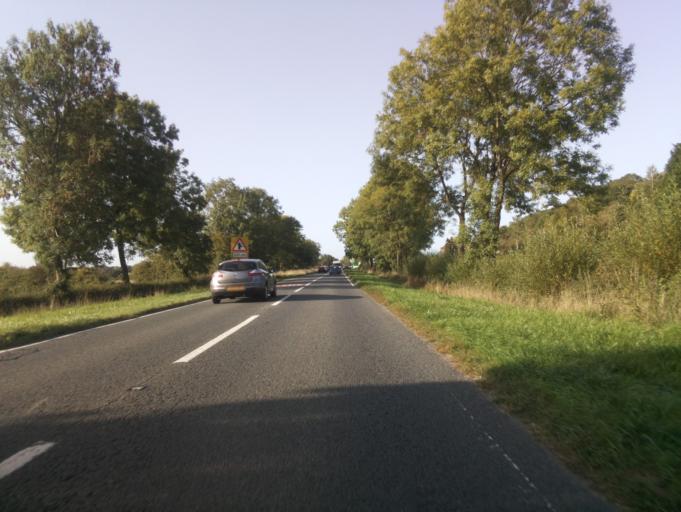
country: GB
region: England
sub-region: Gloucestershire
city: Gloucester
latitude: 51.9358
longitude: -2.2953
